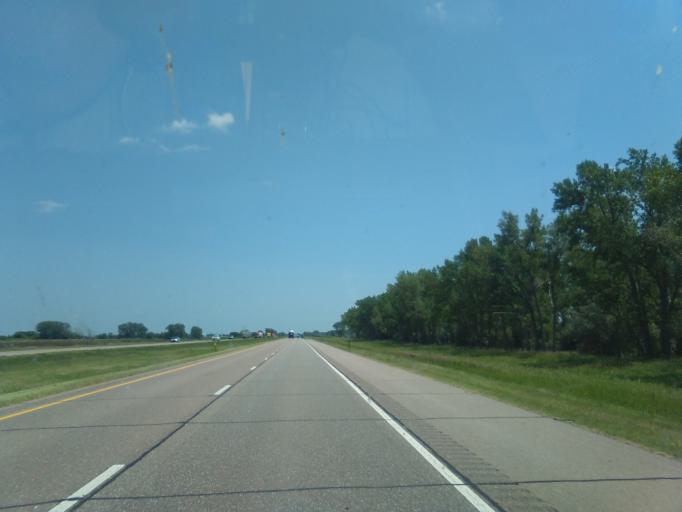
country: US
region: Nebraska
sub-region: Dawson County
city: Cozad
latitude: 40.8754
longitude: -100.0605
